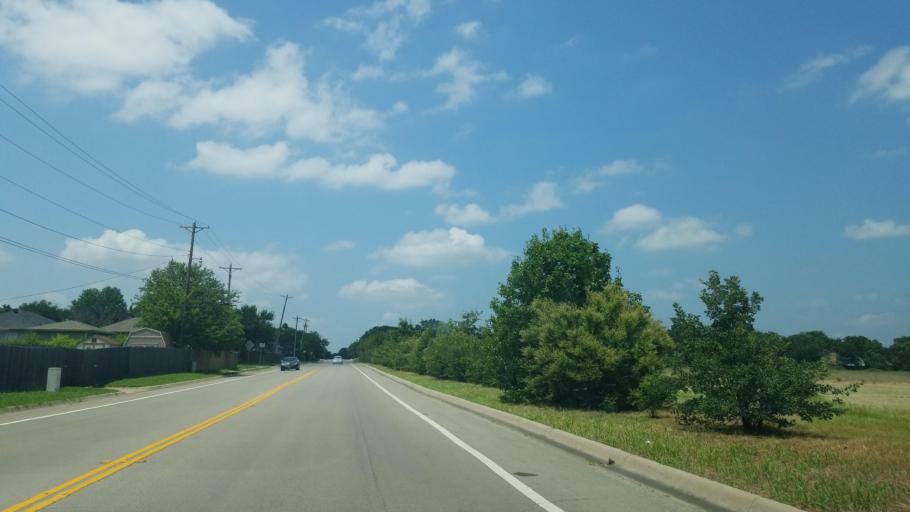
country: US
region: Texas
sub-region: Denton County
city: Denton
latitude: 33.2229
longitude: -97.0977
